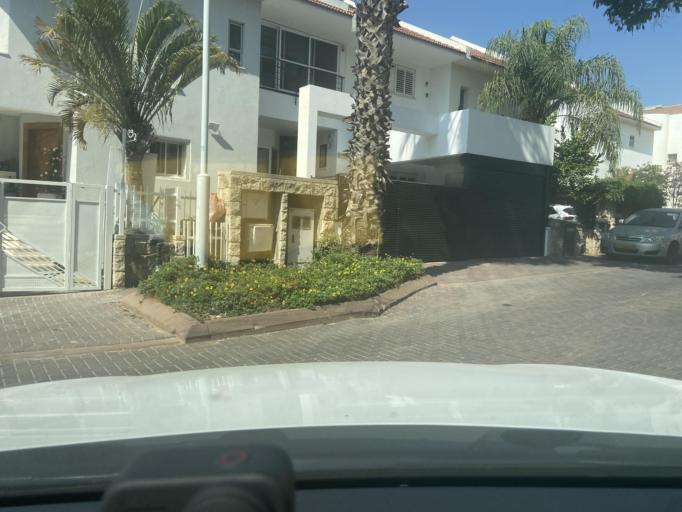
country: IL
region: Central District
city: Yehud
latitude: 32.0358
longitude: 34.8828
